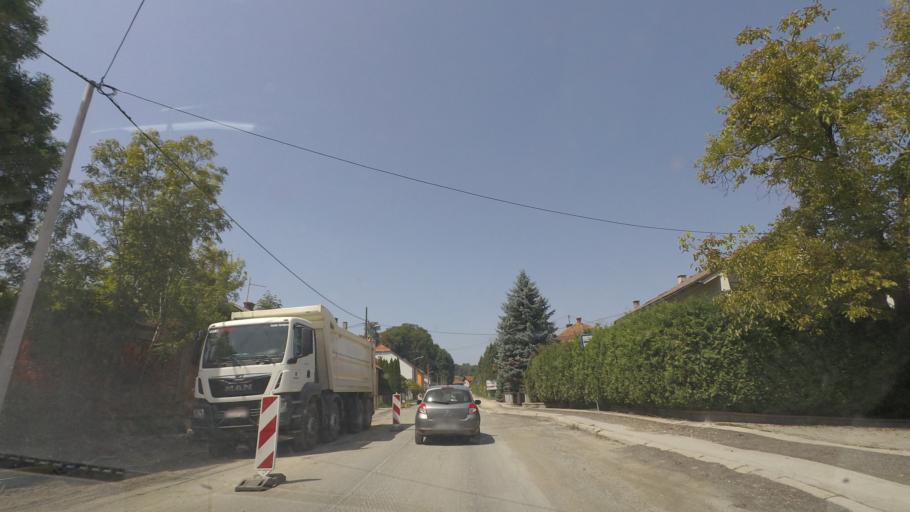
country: HR
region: Karlovacka
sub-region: Grad Karlovac
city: Karlovac
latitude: 45.4998
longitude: 15.5251
